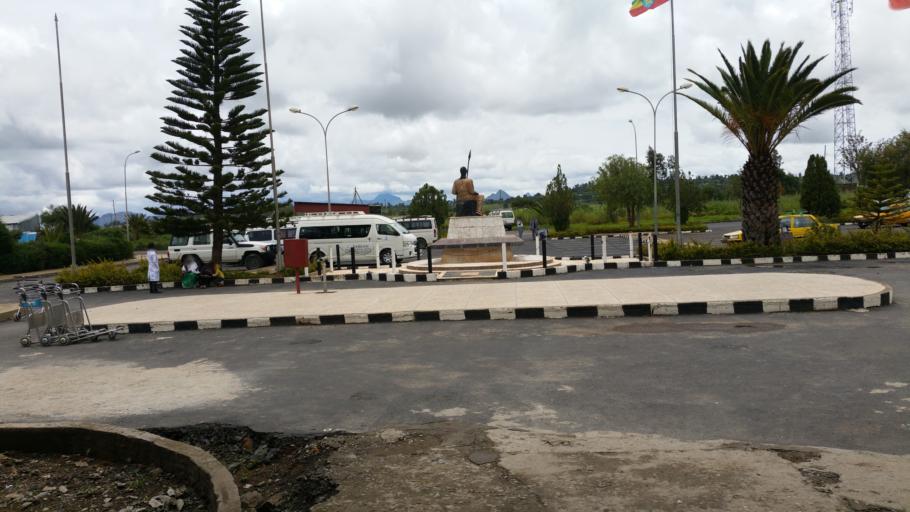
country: ET
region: Tigray
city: Aksum
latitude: 14.1445
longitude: 38.7770
